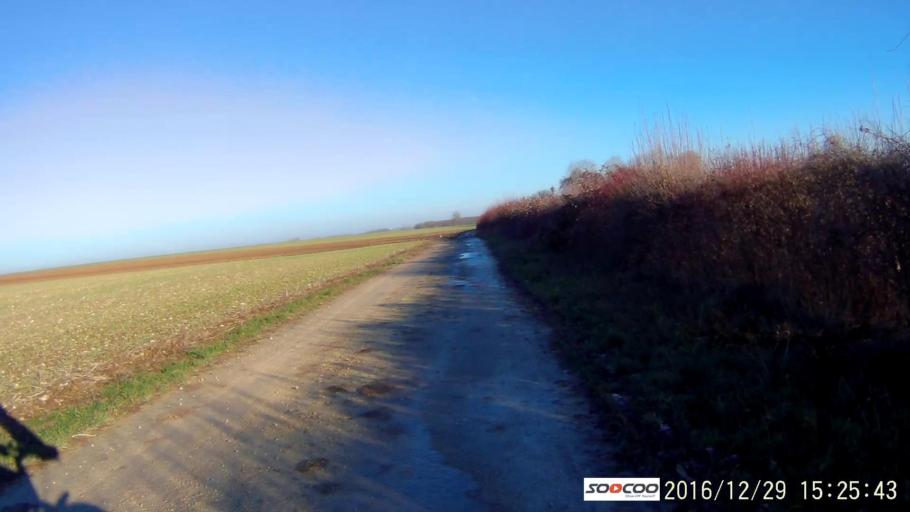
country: FR
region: Centre
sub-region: Departement de l'Indre
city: Neuvy-Pailloux
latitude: 46.9368
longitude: 1.8234
